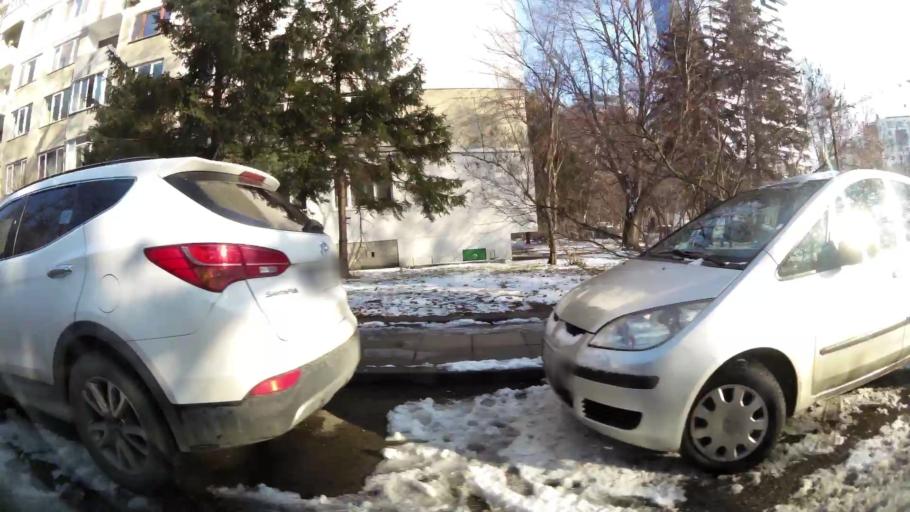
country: BG
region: Sofia-Capital
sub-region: Stolichna Obshtina
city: Sofia
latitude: 42.6677
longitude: 23.3435
